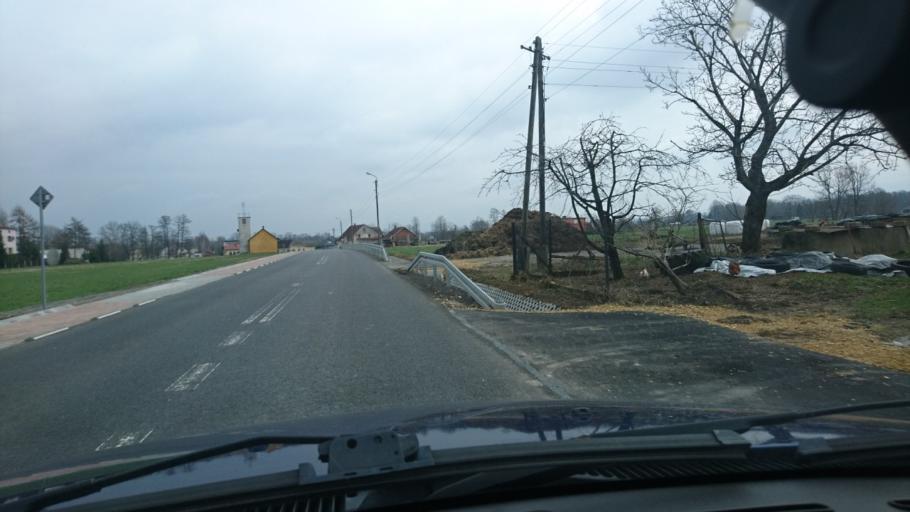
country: PL
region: Silesian Voivodeship
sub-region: Powiat bielski
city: Bronow
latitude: 49.8762
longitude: 18.9110
